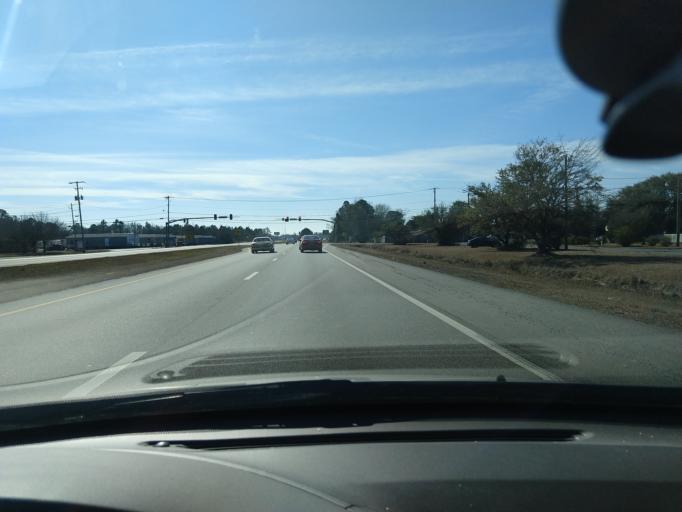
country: US
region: Mississippi
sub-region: Jackson County
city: Moss Point
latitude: 30.4036
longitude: -88.5097
